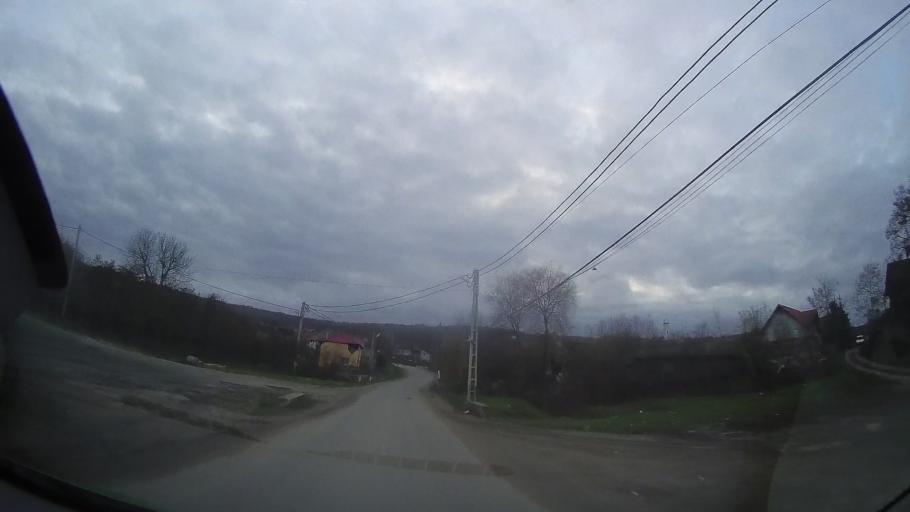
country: RO
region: Cluj
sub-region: Comuna Palatca
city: Palatca
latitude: 46.8395
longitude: 23.9855
